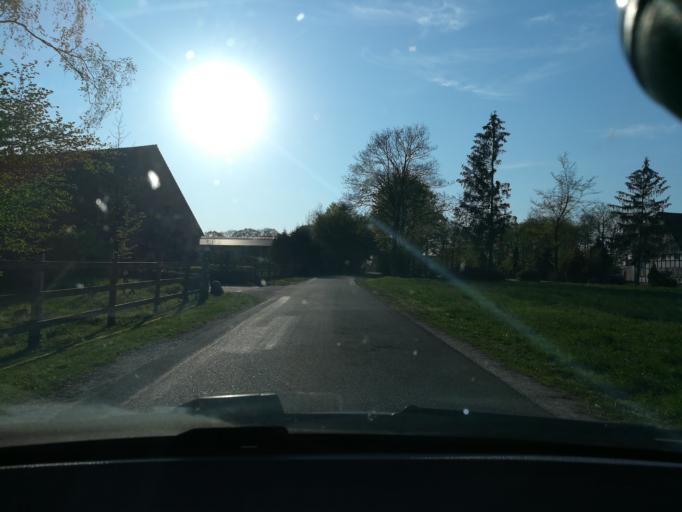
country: DE
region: North Rhine-Westphalia
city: Versmold
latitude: 52.0203
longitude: 8.1101
